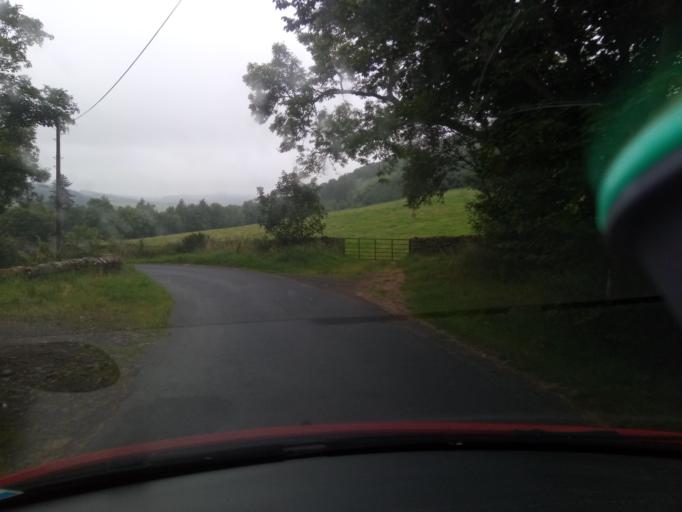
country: GB
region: Scotland
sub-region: The Scottish Borders
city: Galashiels
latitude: 55.6392
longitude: -2.8251
